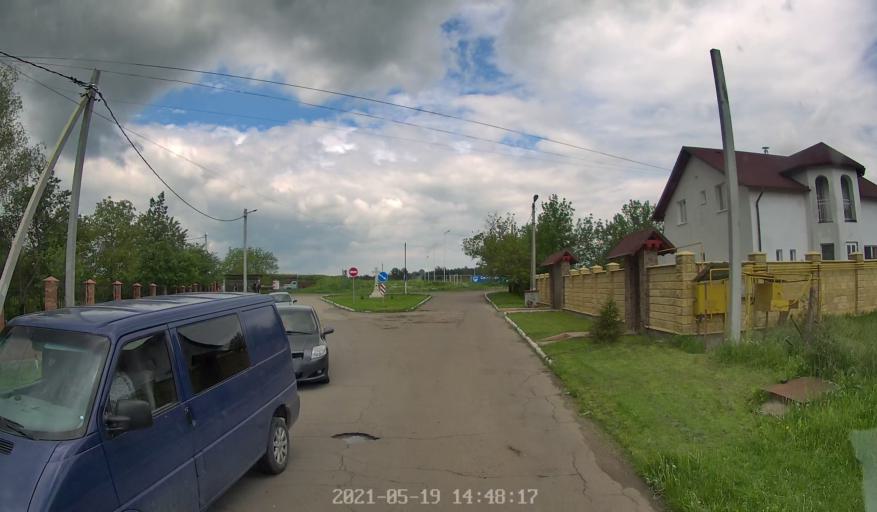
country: MD
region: Chisinau
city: Stauceni
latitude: 47.0450
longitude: 28.9594
